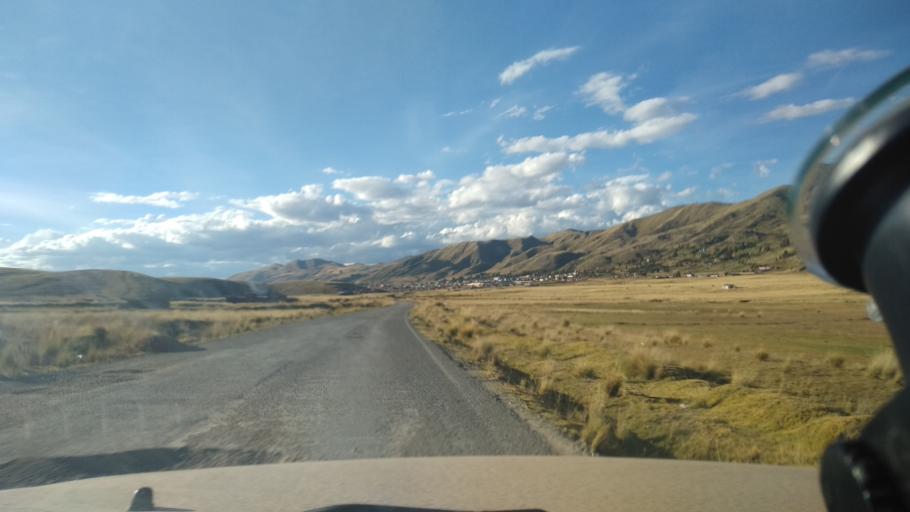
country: PE
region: Cusco
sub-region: Provincia de Canas
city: Chignayhua
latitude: -14.2393
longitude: -71.4327
